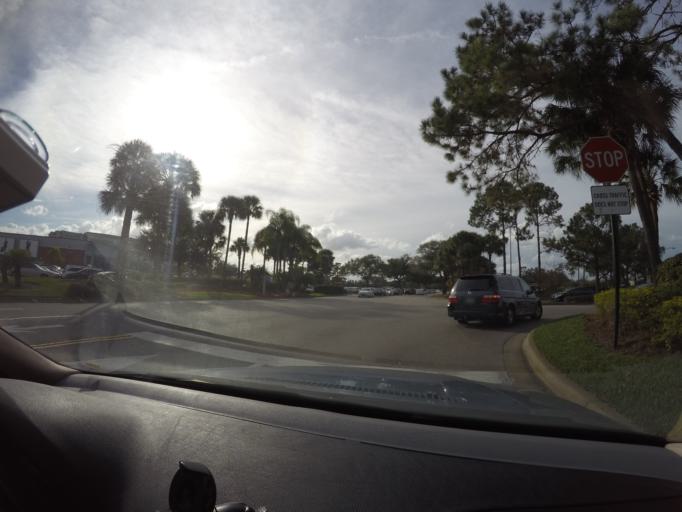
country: US
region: Florida
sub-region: Orange County
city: Sky Lake
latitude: 28.4481
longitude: -81.3936
